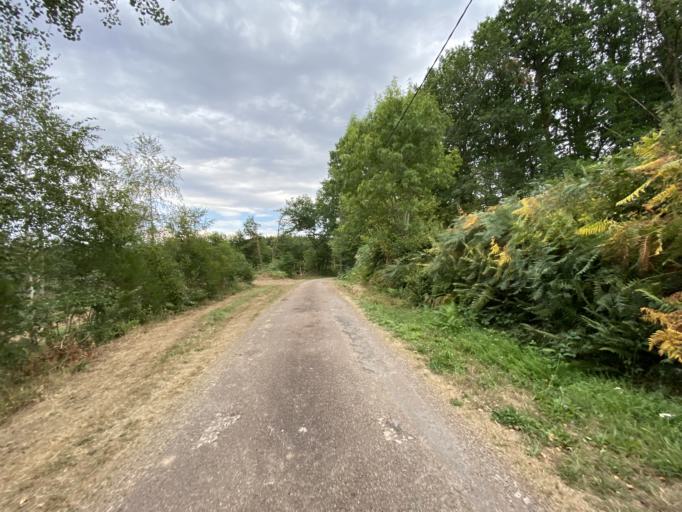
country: FR
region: Bourgogne
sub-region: Departement de la Cote-d'Or
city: Saulieu
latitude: 47.2718
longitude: 4.1423
